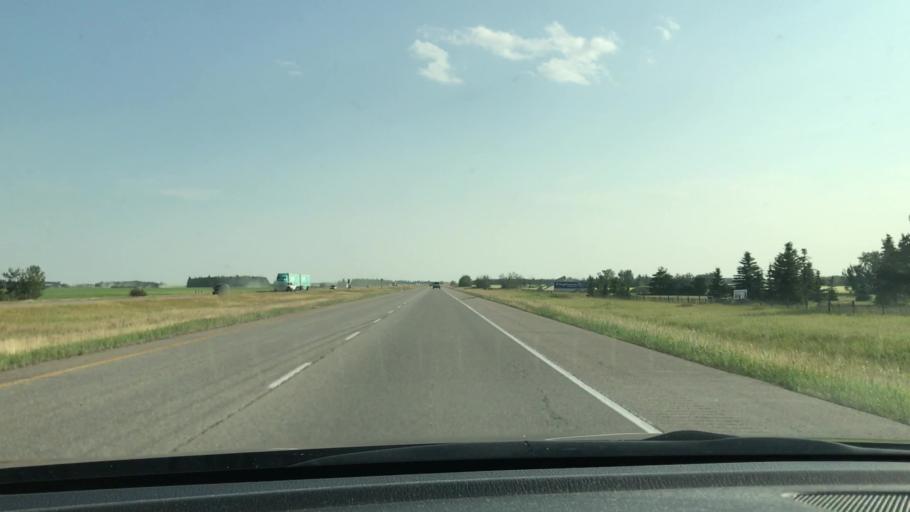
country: CA
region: Alberta
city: Leduc
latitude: 53.2185
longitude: -113.5826
